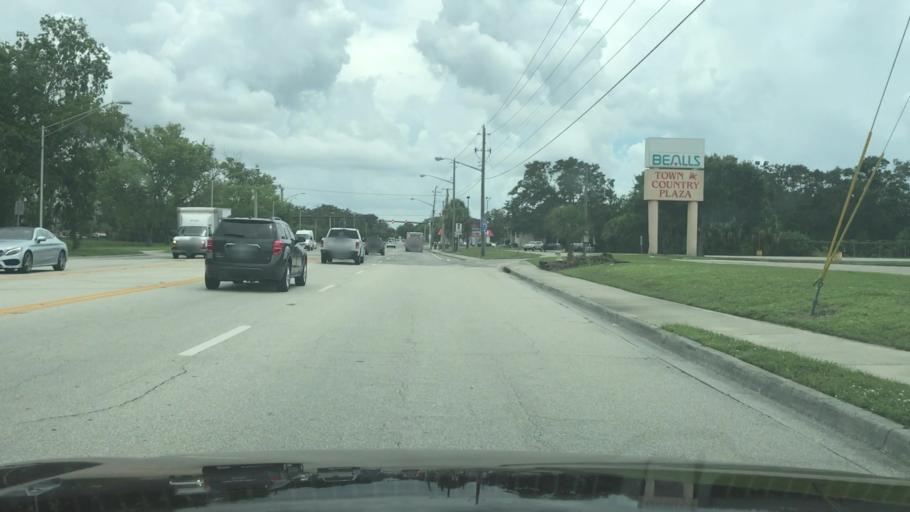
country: US
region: Florida
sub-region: Sarasota County
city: Kensington Park
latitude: 27.3395
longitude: -82.4974
